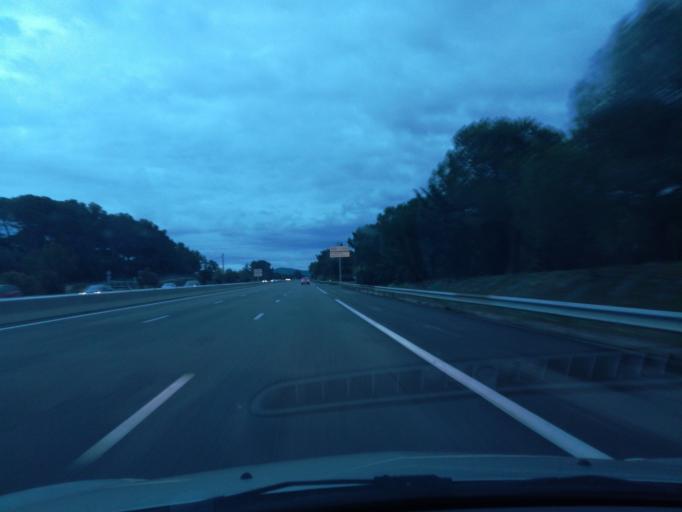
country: FR
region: Provence-Alpes-Cote d'Azur
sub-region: Departement du Var
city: Puget-sur-Argens
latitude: 43.4617
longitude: 6.7134
